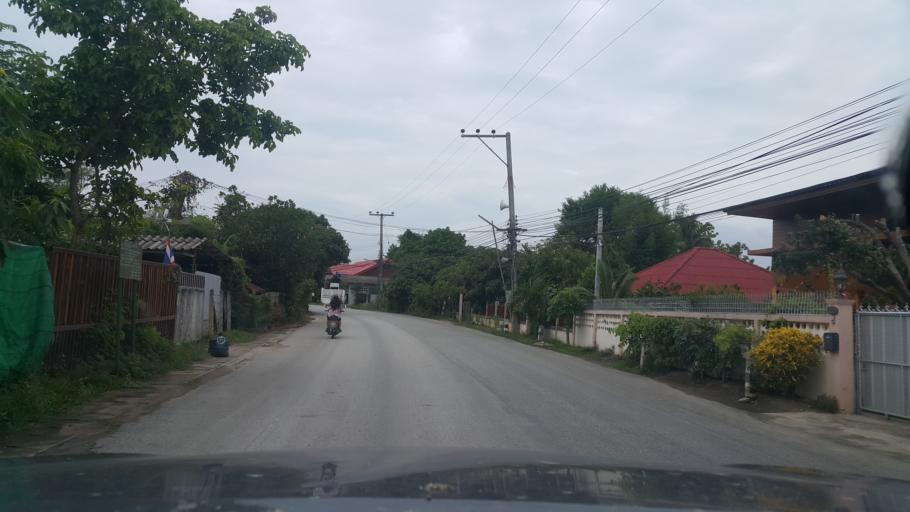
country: TH
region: Chiang Mai
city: San Pa Tong
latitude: 18.6533
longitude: 98.8372
